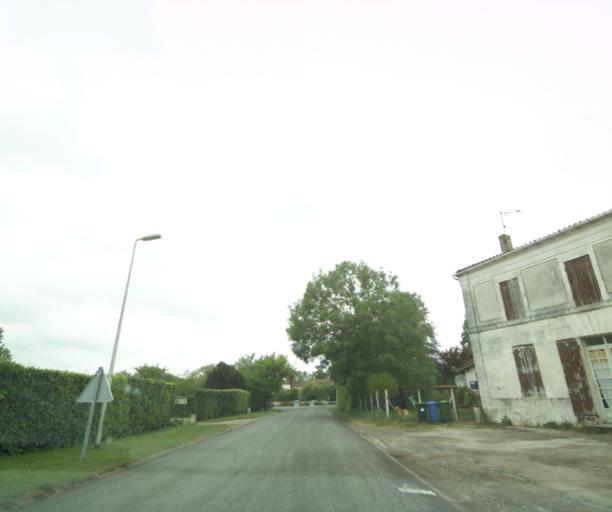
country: FR
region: Poitou-Charentes
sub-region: Departement de la Charente-Maritime
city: Cherac
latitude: 45.6846
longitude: -0.4899
